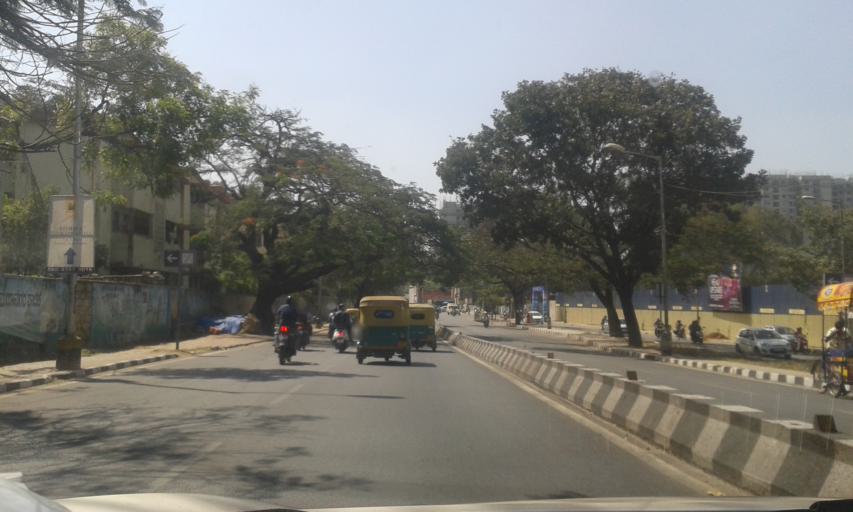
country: IN
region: Karnataka
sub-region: Bangalore Urban
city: Bangalore
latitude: 12.9810
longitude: 77.5644
